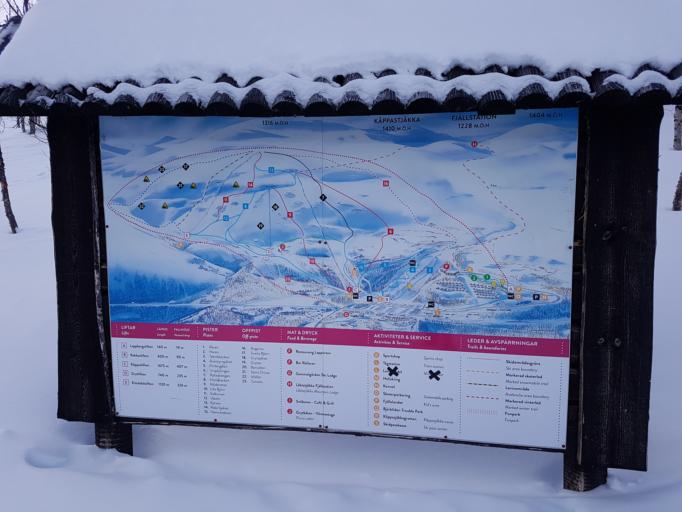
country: NO
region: Troms
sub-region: Bardu
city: Setermoen
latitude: 68.4066
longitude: 18.6740
